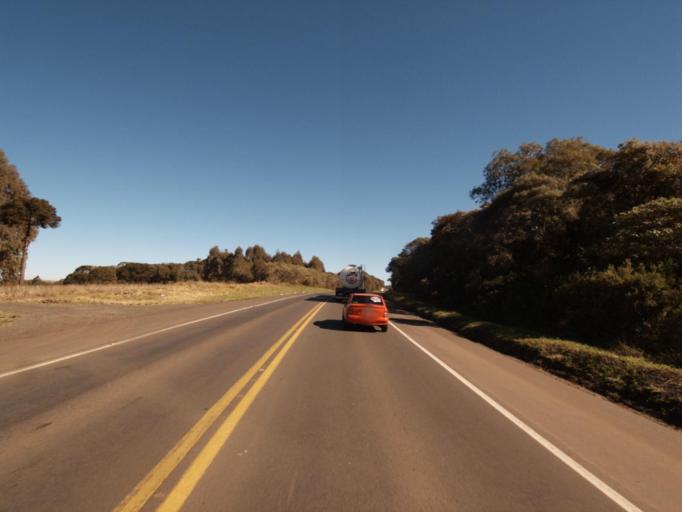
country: BR
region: Santa Catarina
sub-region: Xanxere
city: Xanxere
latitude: -26.8714
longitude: -52.2760
